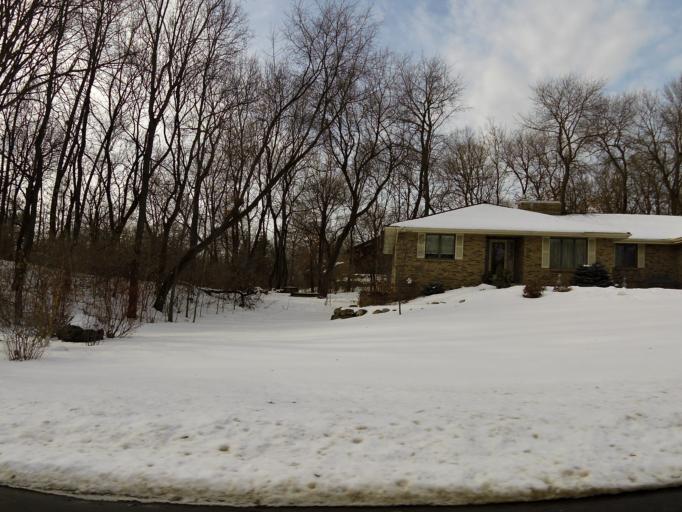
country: US
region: Minnesota
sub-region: Dakota County
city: Lakeville
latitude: 44.6824
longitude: -93.2727
